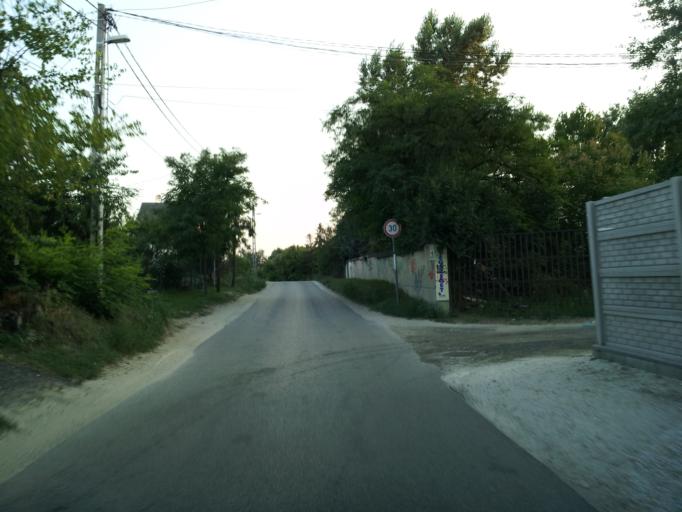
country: HU
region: Pest
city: Szigetszentmiklos
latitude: 47.3273
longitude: 19.0316
